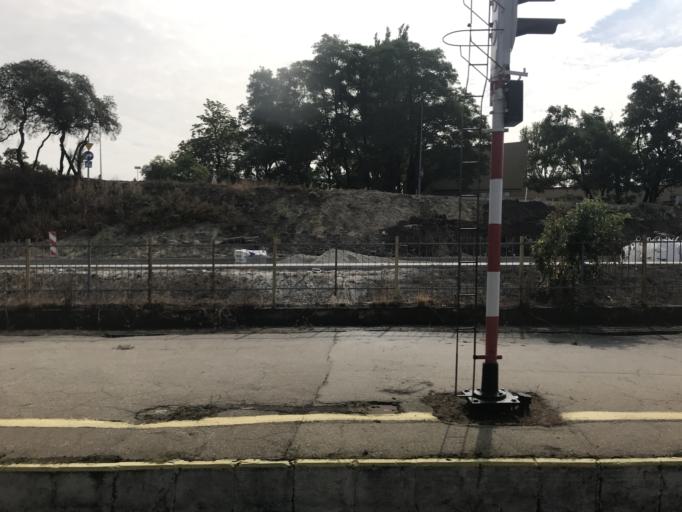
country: PL
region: Kujawsko-Pomorskie
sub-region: Powiat inowroclawski
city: Inowroclaw
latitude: 52.8067
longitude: 18.2447
